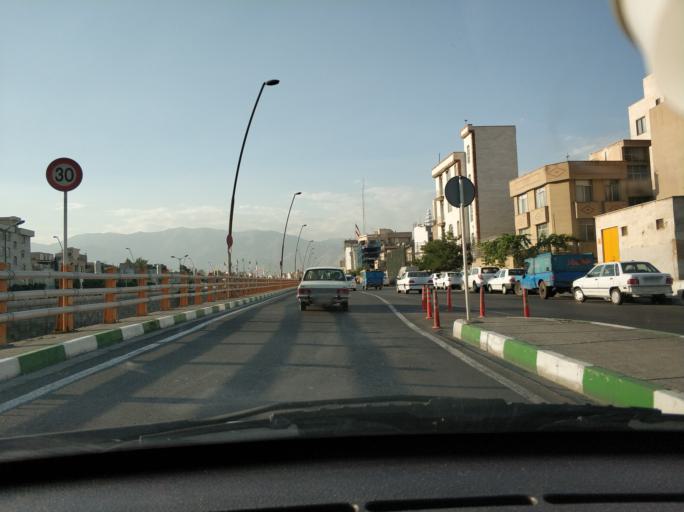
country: IR
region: Tehran
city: Tehran
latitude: 35.6995
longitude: 51.4574
